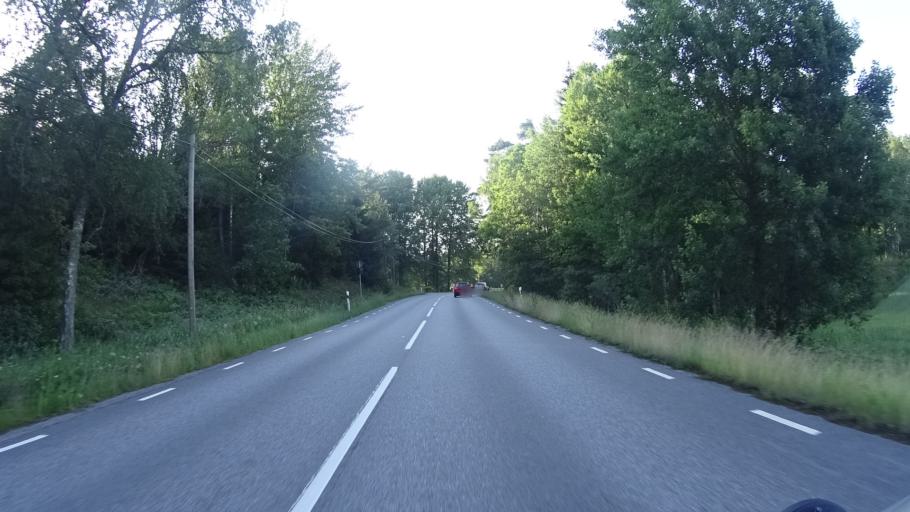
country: SE
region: Stockholm
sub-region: Sodertalje Kommun
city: Pershagen
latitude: 59.1151
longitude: 17.6402
